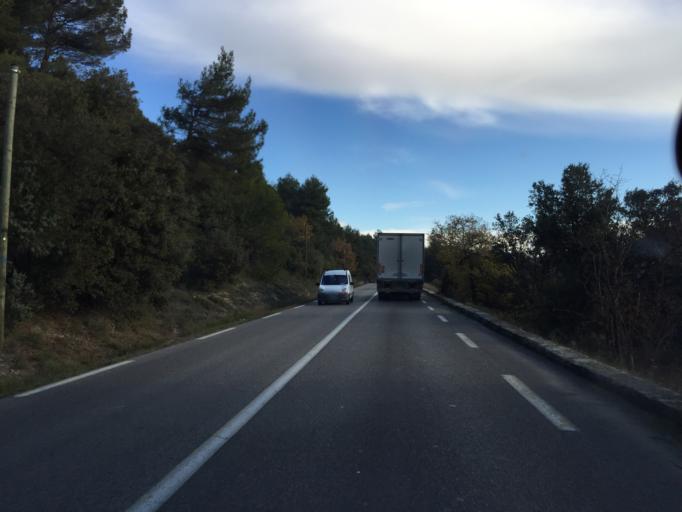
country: FR
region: Provence-Alpes-Cote d'Azur
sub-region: Departement du Vaucluse
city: Goult
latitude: 43.8610
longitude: 5.2225
